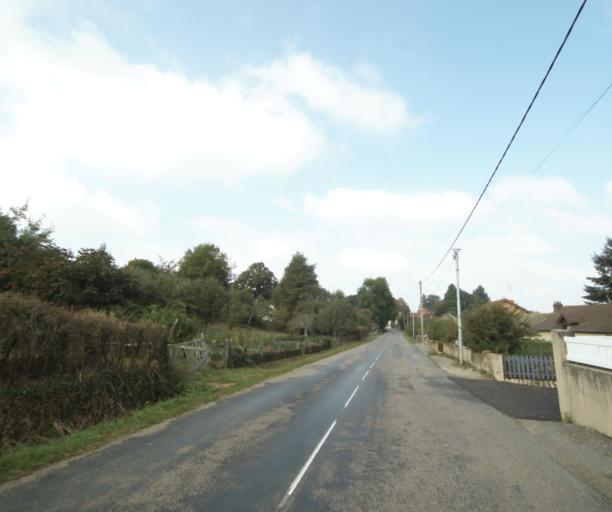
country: FR
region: Bourgogne
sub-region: Departement de Saone-et-Loire
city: Charolles
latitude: 46.4299
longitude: 4.2996
